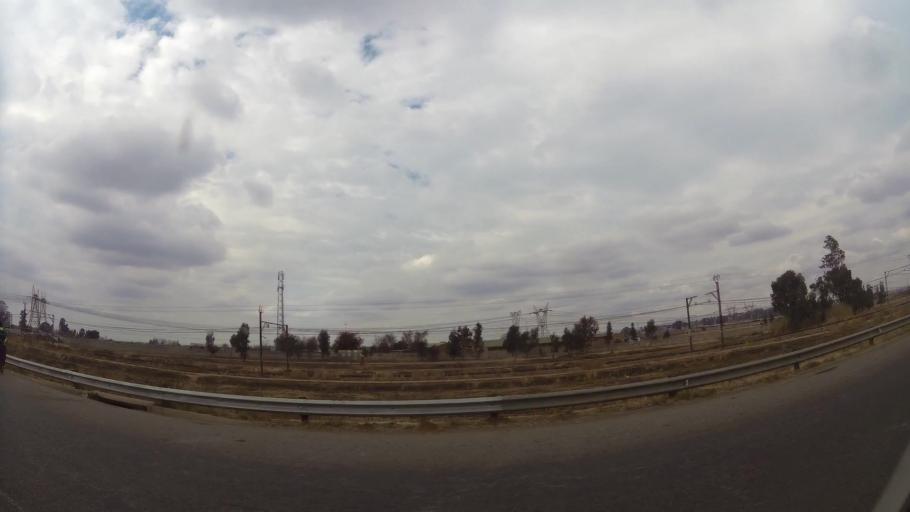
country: ZA
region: Gauteng
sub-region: Ekurhuleni Metropolitan Municipality
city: Germiston
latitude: -26.3603
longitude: 28.1189
